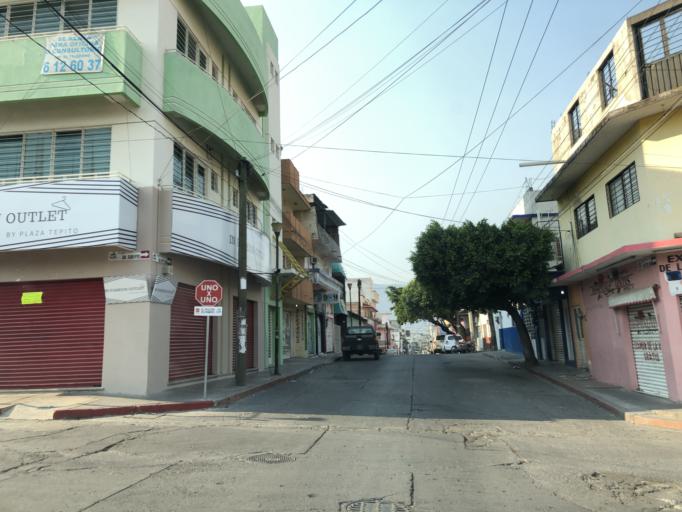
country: MX
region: Chiapas
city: Tuxtla Gutierrez
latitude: 16.7517
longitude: -93.1218
